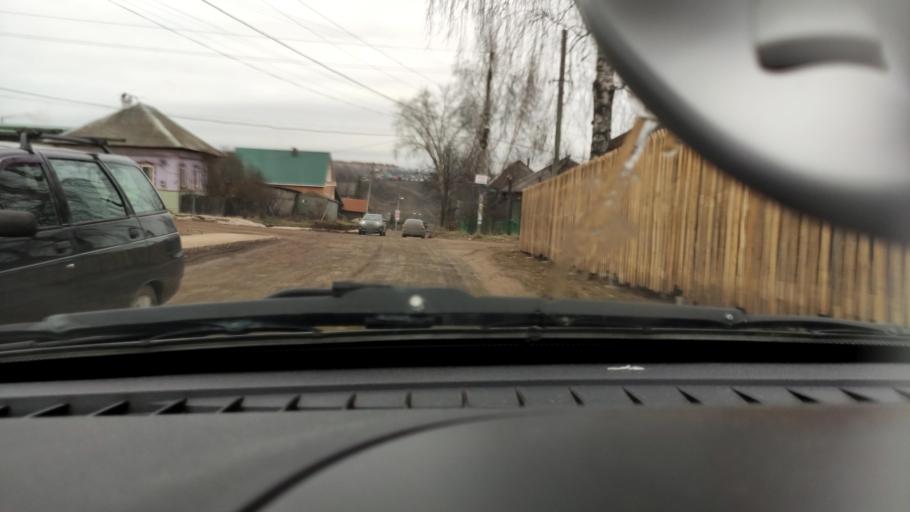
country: RU
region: Perm
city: Perm
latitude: 58.0269
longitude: 56.3368
